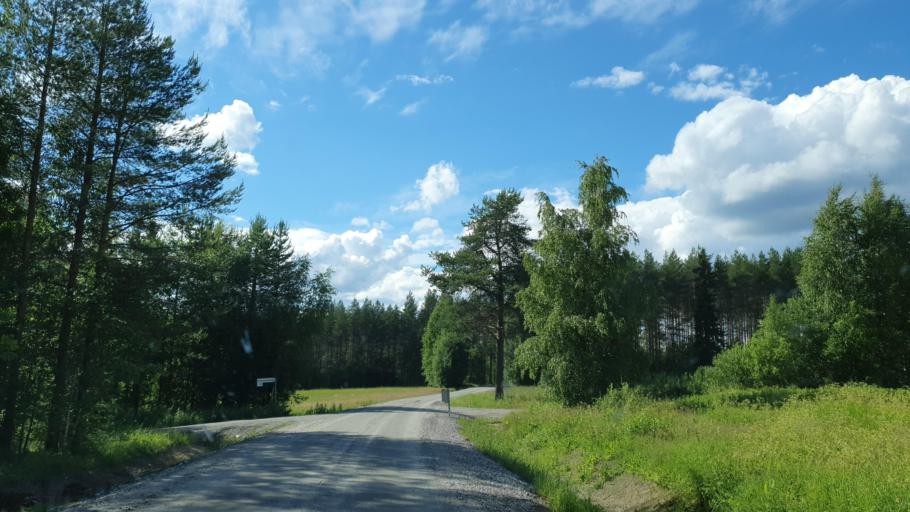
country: FI
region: Kainuu
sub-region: Kehys-Kainuu
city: Kuhmo
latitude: 64.1470
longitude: 29.7552
